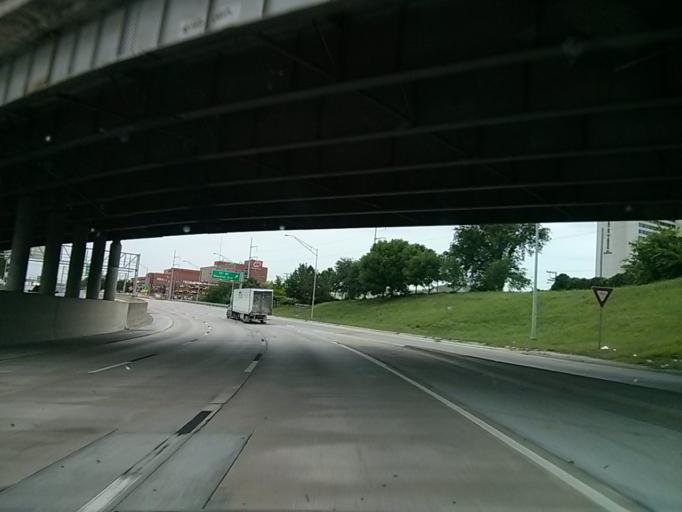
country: US
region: Oklahoma
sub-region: Tulsa County
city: Tulsa
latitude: 36.1451
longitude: -95.9942
